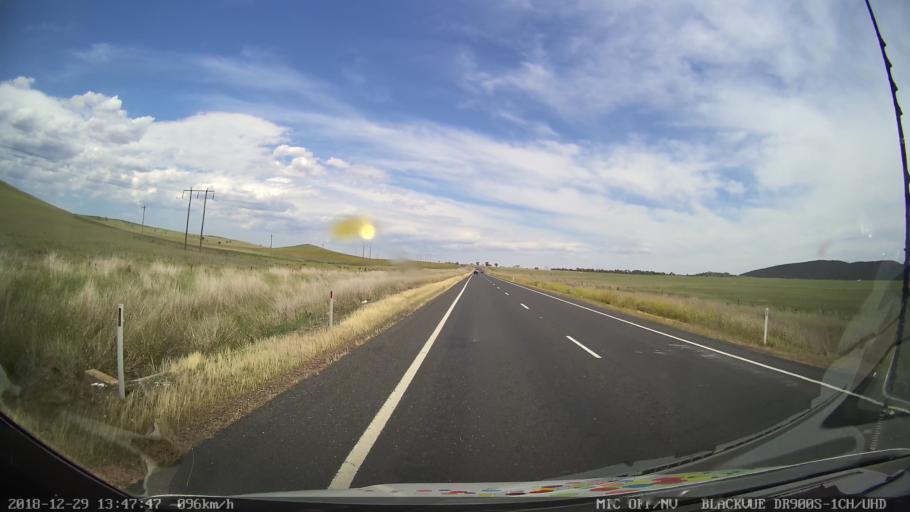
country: AU
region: New South Wales
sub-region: Cooma-Monaro
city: Cooma
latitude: -36.1314
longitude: 149.1445
